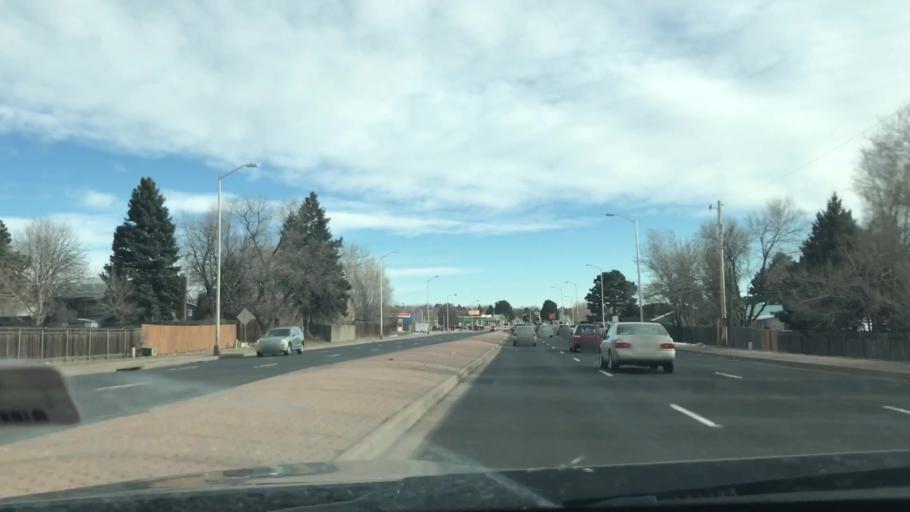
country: US
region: Colorado
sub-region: El Paso County
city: Cimarron Hills
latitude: 38.8964
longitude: -104.7605
